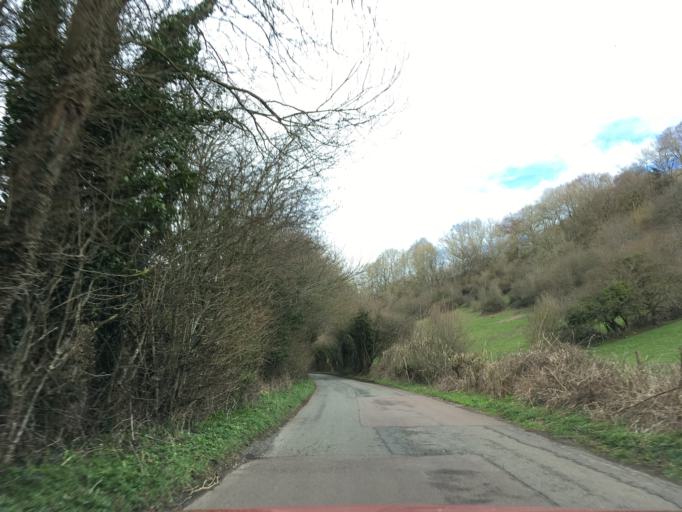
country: GB
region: England
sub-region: Gloucestershire
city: Coleford
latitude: 51.7828
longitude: -2.6318
